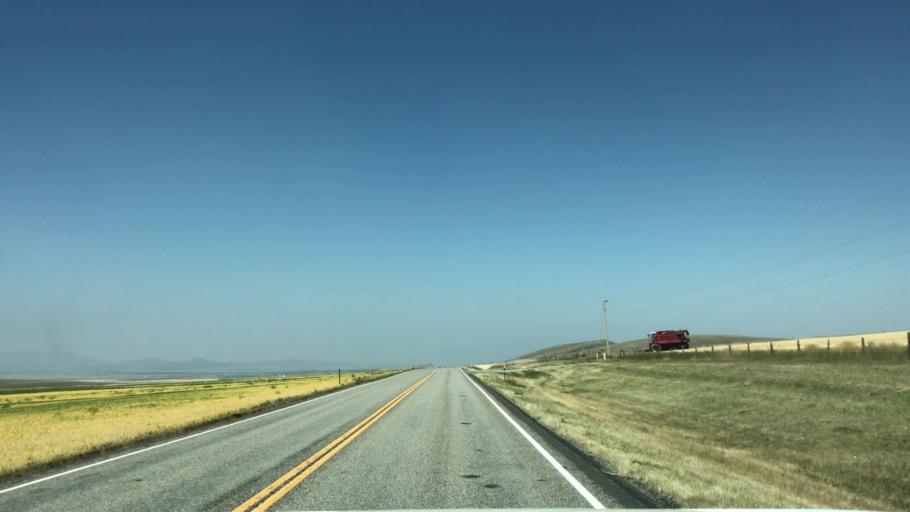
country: US
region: Montana
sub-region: Gallatin County
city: Three Forks
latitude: 46.0054
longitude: -111.5836
